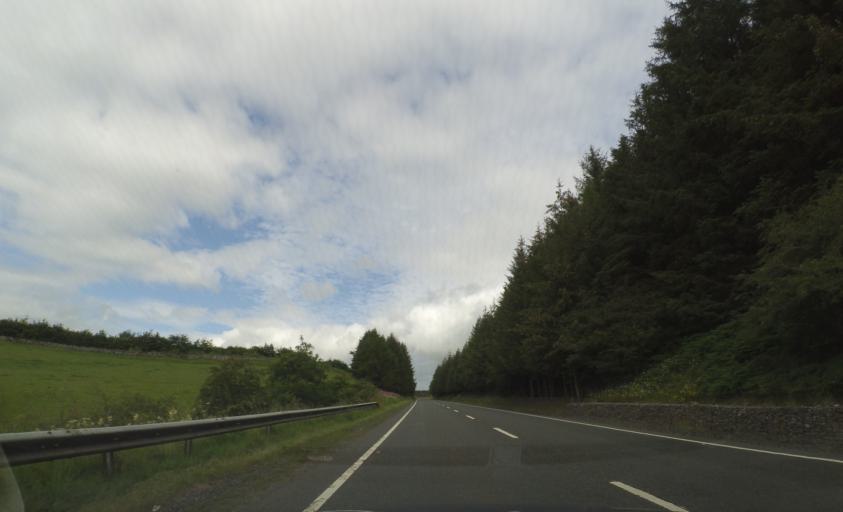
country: GB
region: Scotland
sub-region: The Scottish Borders
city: Selkirk
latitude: 55.5044
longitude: -2.8364
